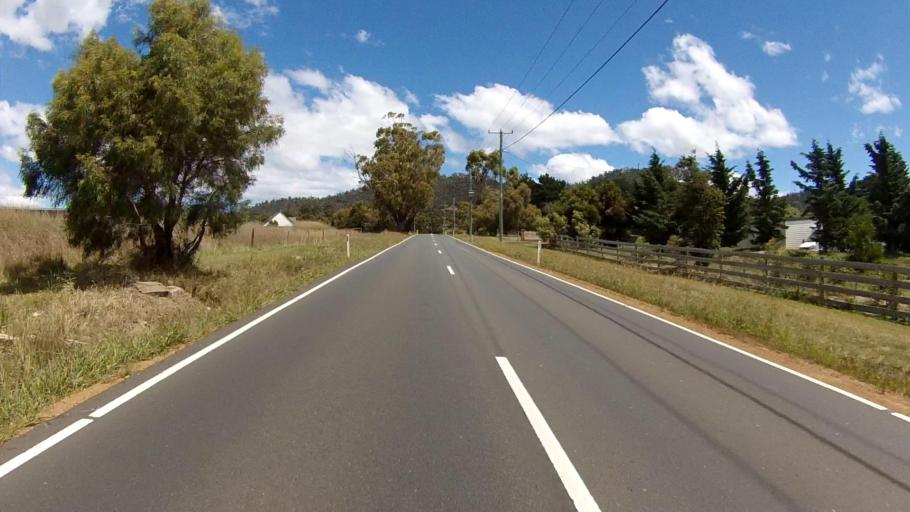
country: AU
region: Tasmania
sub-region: Clarence
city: Acton Park
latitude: -42.8517
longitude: 147.4744
